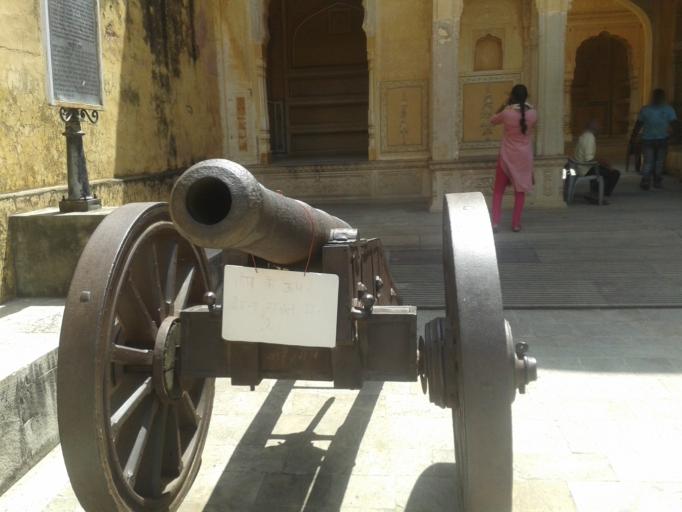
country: IN
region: Rajasthan
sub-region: Jaipur
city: Jaipur
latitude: 26.9376
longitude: 75.8156
